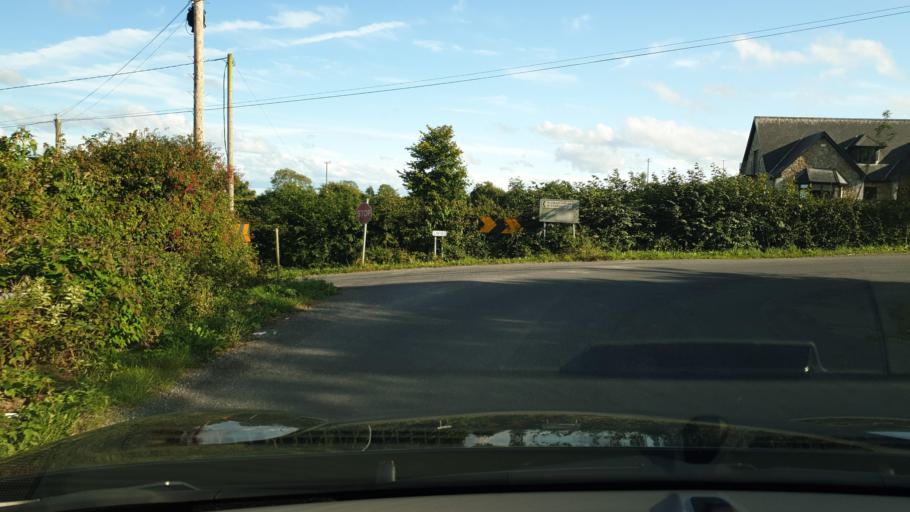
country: IE
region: Leinster
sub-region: An Mhi
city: Stamullin
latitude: 53.6067
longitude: -6.2892
